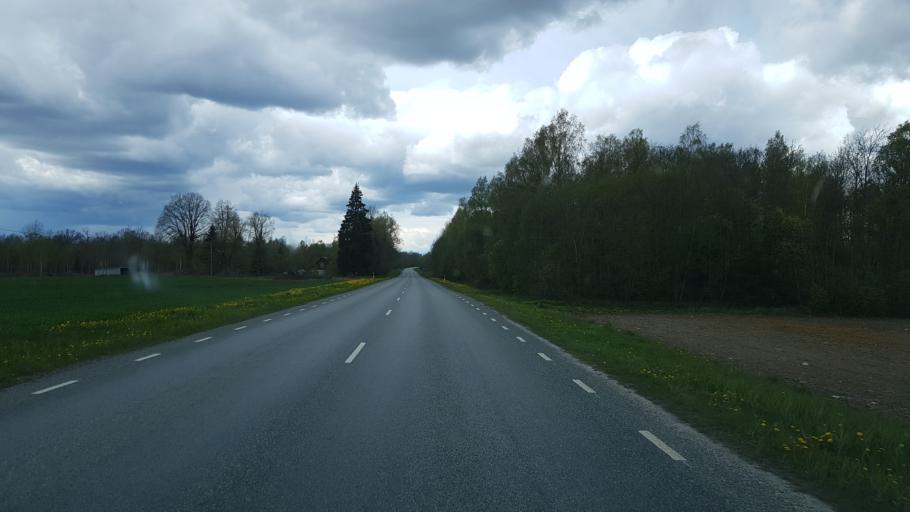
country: EE
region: Paernumaa
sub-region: Audru vald
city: Audru
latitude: 58.5072
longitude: 24.1110
